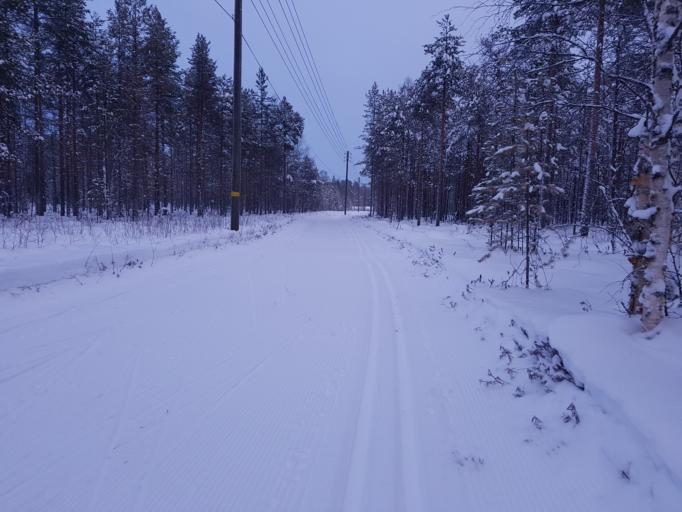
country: FI
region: Kainuu
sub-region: Kehys-Kainuu
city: Kuhmo
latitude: 64.1160
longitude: 29.5700
